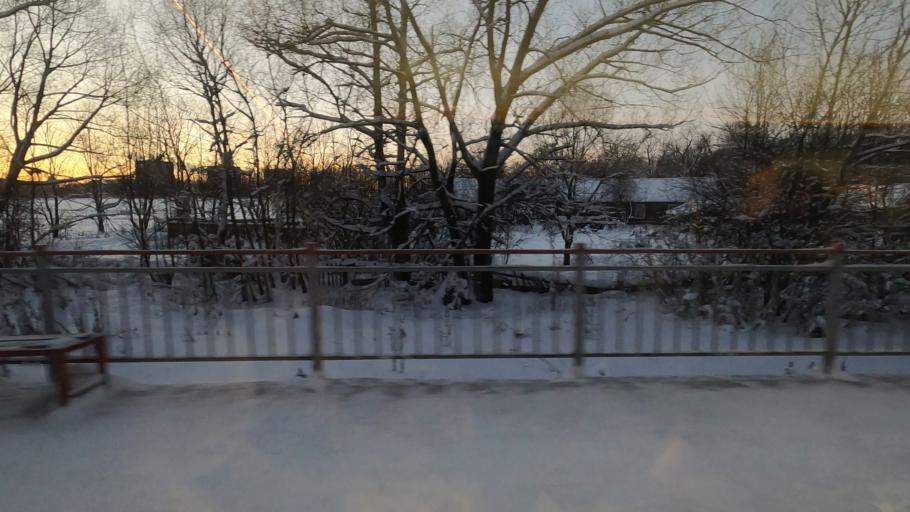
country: RU
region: Moskovskaya
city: Lugovaya
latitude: 56.0492
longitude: 37.4927
